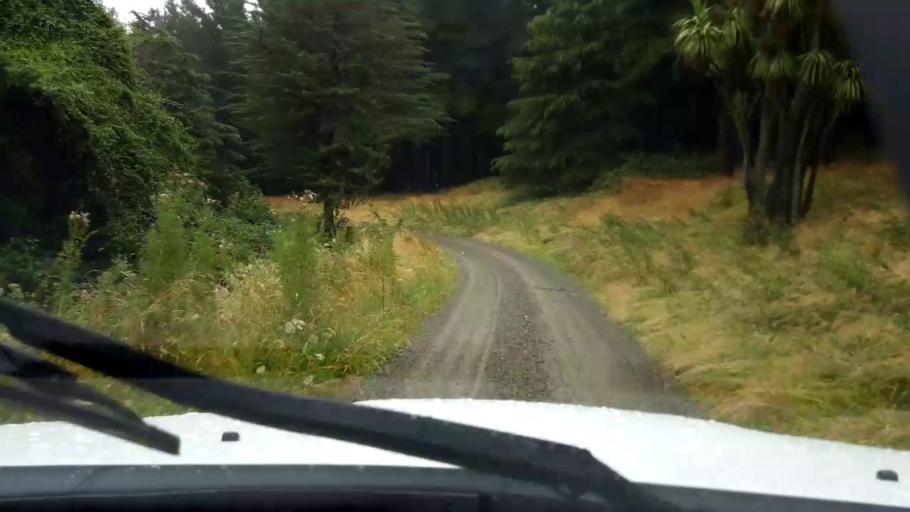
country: NZ
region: Canterbury
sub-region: Timaru District
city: Pleasant Point
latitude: -44.1825
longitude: 171.1024
